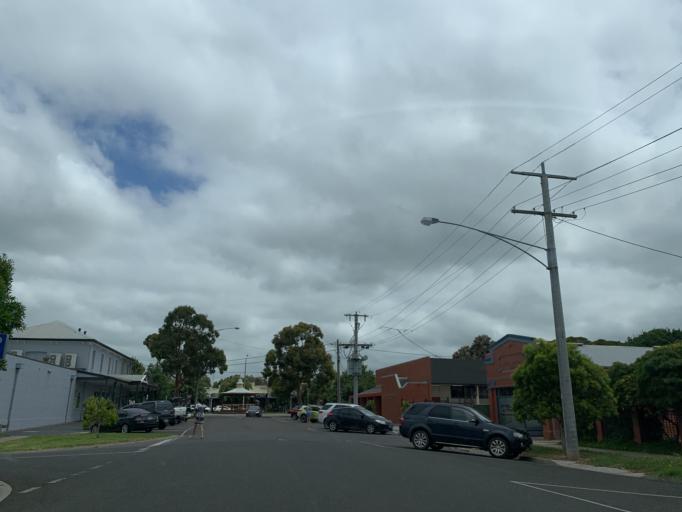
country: AU
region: Victoria
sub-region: Wellington
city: Sale
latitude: -37.9662
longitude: 146.9769
